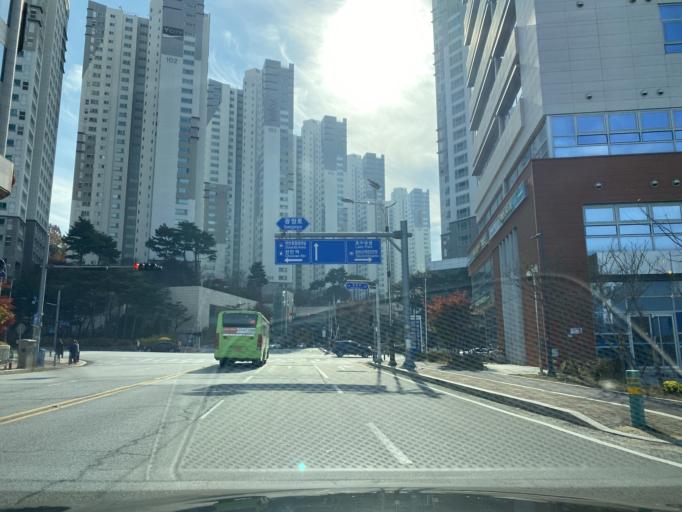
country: KR
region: Chungcheongnam-do
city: Cheonan
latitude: 36.7981
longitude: 127.1079
